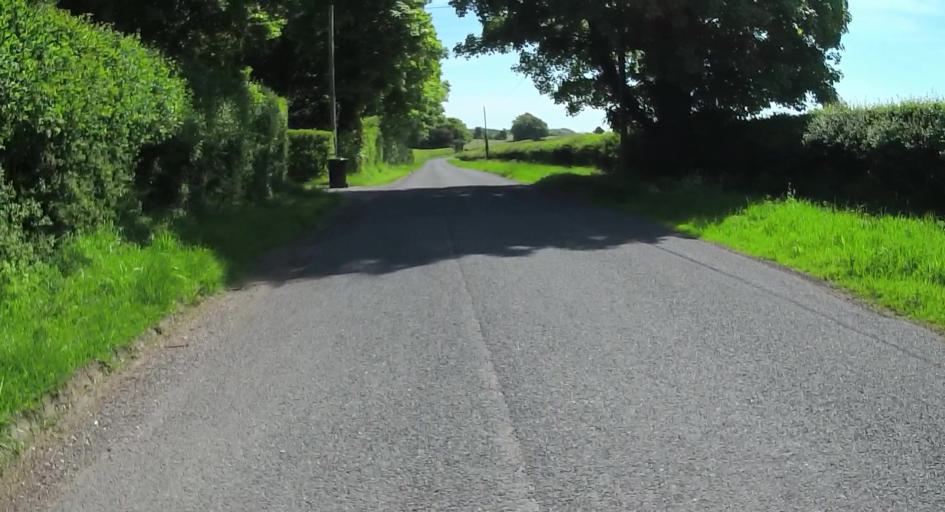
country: GB
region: England
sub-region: Hampshire
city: Four Marks
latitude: 51.1642
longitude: -1.1364
